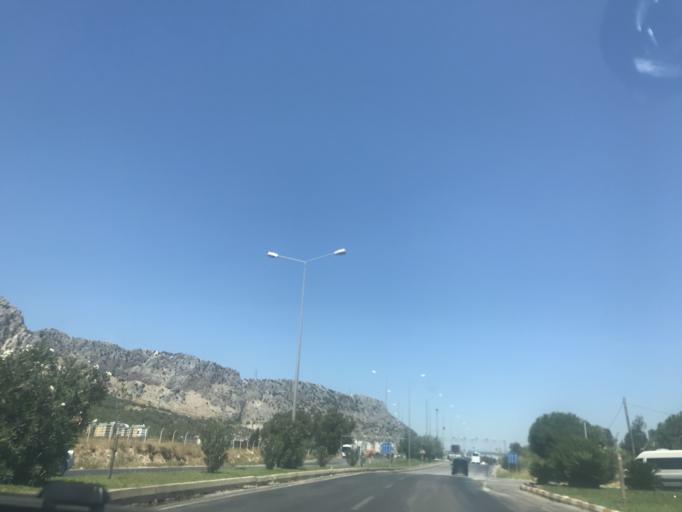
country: TR
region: Antalya
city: Cakirlar
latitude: 36.8333
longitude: 30.5954
